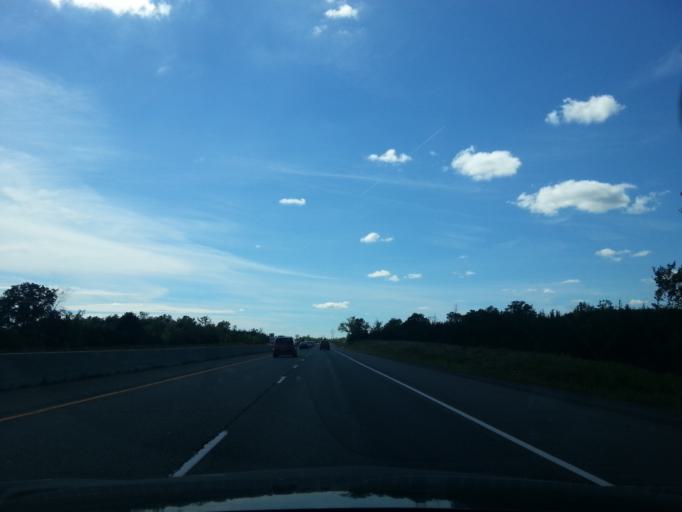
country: CA
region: Ontario
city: Belleville
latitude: 44.2183
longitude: -77.2533
